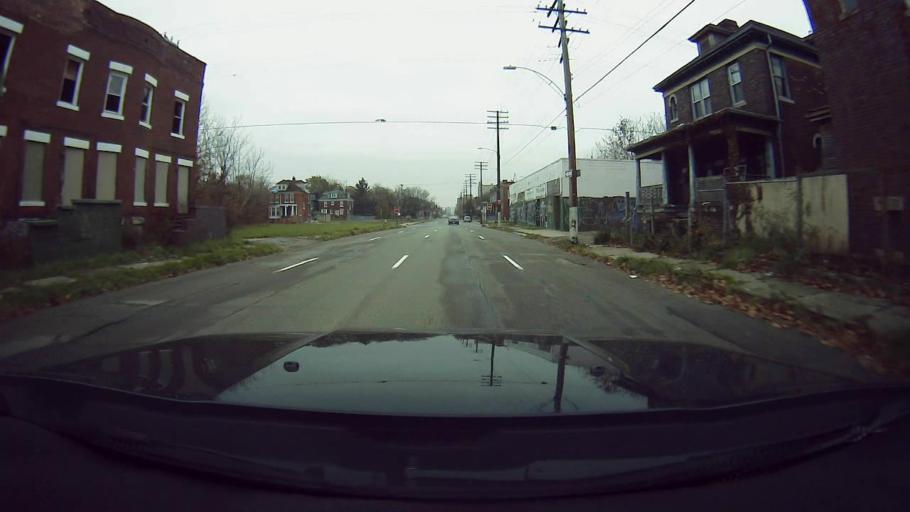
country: US
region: Michigan
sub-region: Wayne County
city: Hamtramck
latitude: 42.3786
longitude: -83.0762
